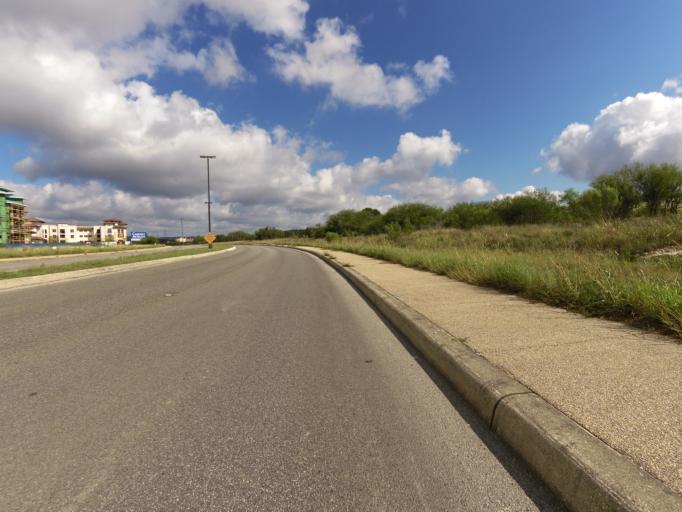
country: US
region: Texas
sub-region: Bexar County
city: Shavano Park
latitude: 29.5954
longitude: -98.5896
